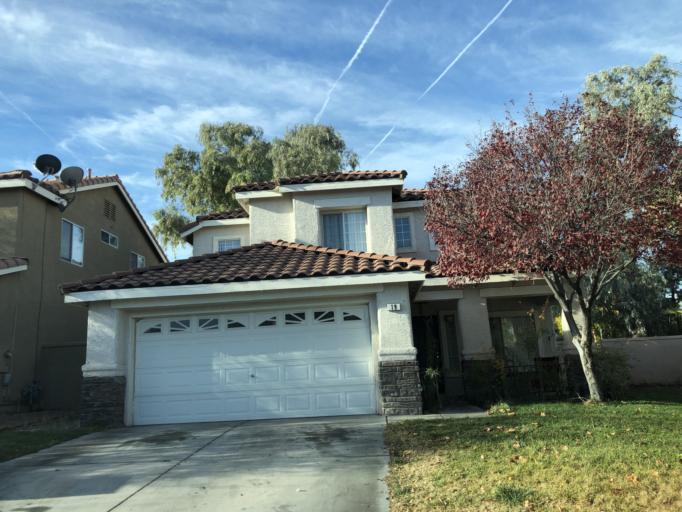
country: US
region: Nevada
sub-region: Clark County
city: Whitney
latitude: 36.0240
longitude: -115.0718
